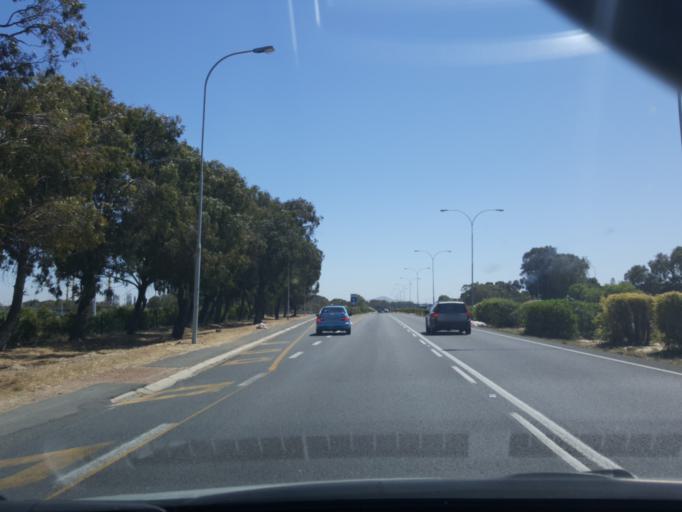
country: ZA
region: Western Cape
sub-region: City of Cape Town
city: Sunset Beach
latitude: -33.8541
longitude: 18.5315
